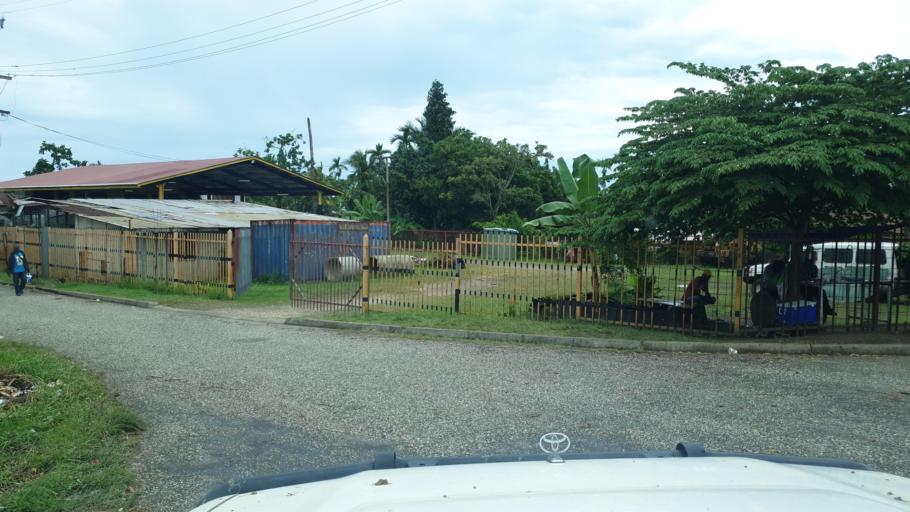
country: PG
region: Gulf
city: Kerema
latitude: -7.9604
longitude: 145.7719
